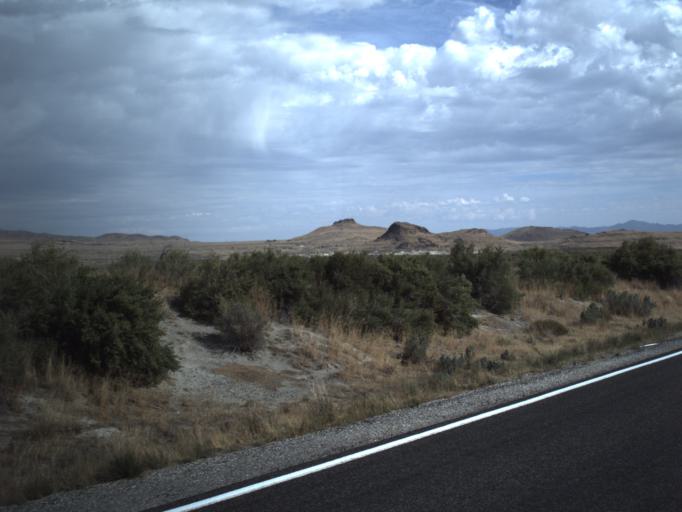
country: US
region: Nevada
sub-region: Elko County
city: West Wendover
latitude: 41.3685
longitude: -114.0393
